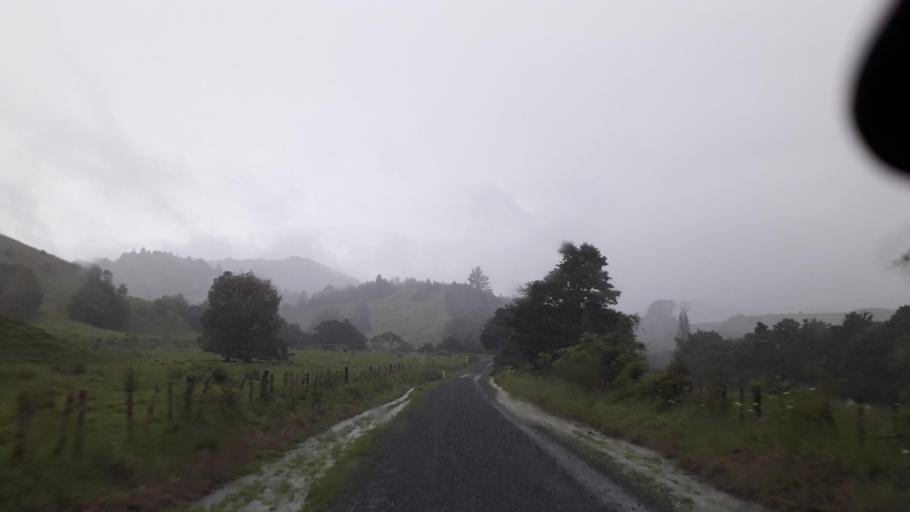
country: NZ
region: Northland
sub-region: Far North District
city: Waimate North
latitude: -35.1513
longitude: 173.7124
